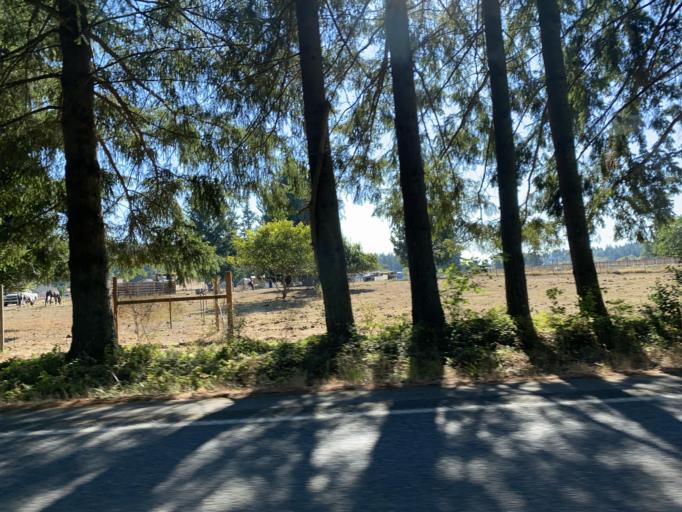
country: US
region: Washington
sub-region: Thurston County
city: Tanglewilde-Thompson Place
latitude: 46.9698
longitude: -122.7642
